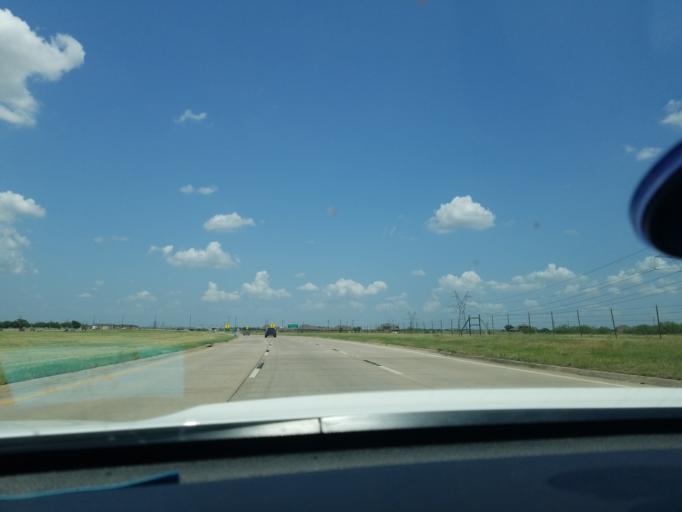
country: US
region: Texas
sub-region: Tarrant County
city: Haslet
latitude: 32.9598
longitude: -97.3034
